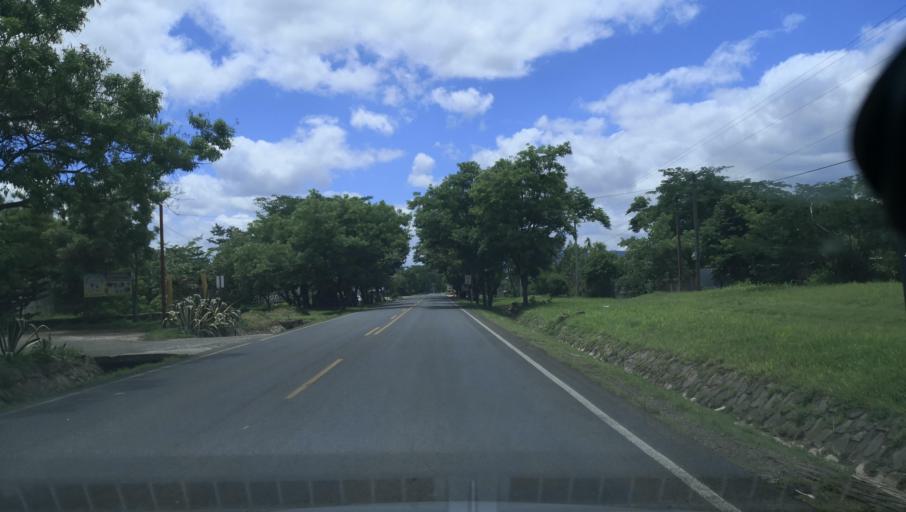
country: NI
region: Esteli
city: Esteli
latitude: 13.1662
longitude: -86.3679
